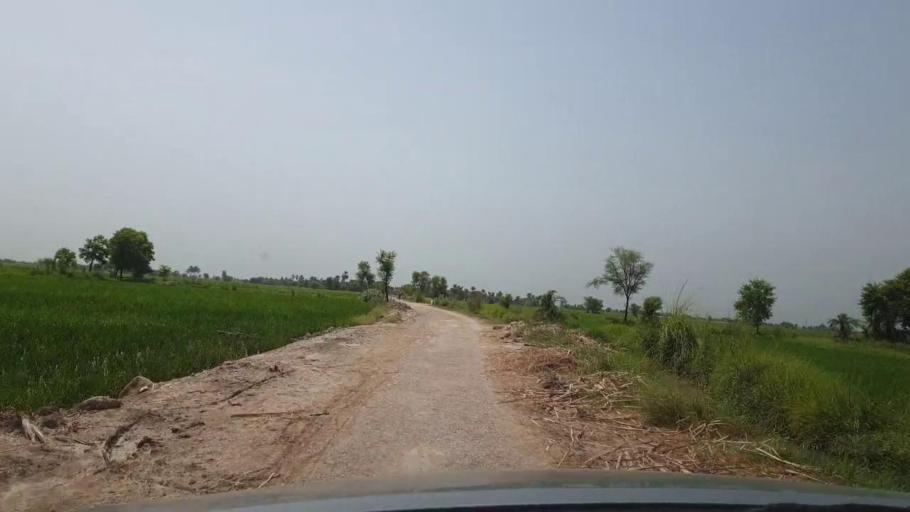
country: PK
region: Sindh
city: Madeji
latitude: 27.7928
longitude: 68.4347
